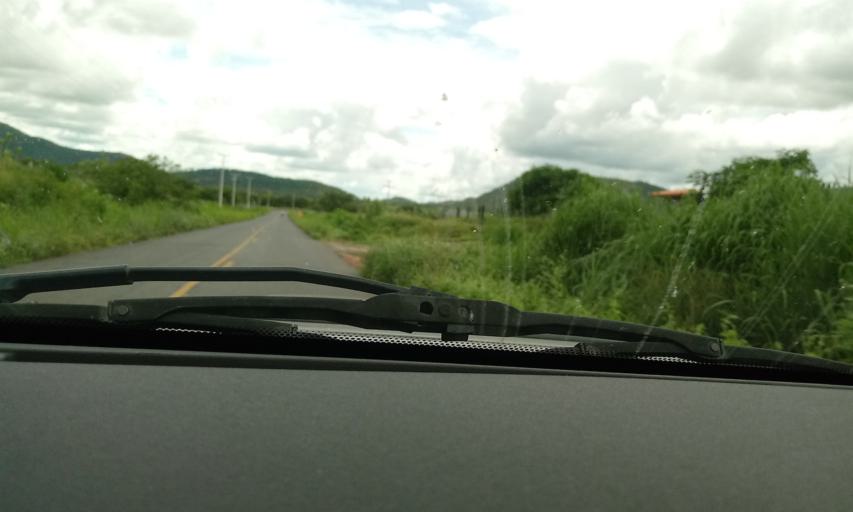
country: BR
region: Bahia
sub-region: Guanambi
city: Guanambi
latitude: -14.1536
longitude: -42.8226
